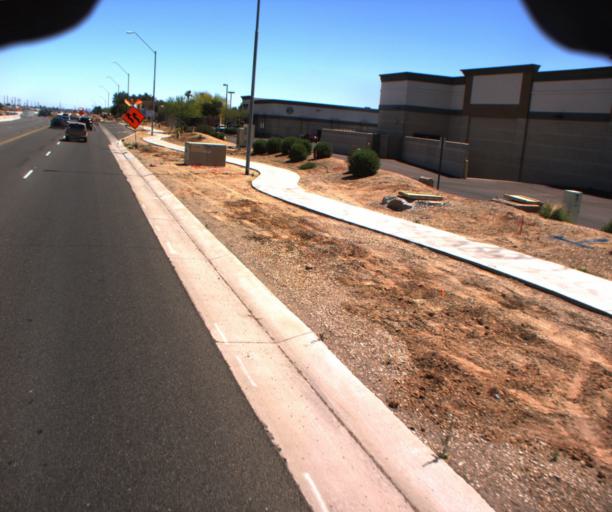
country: US
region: Arizona
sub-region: Maricopa County
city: Surprise
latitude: 33.6405
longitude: -112.3530
